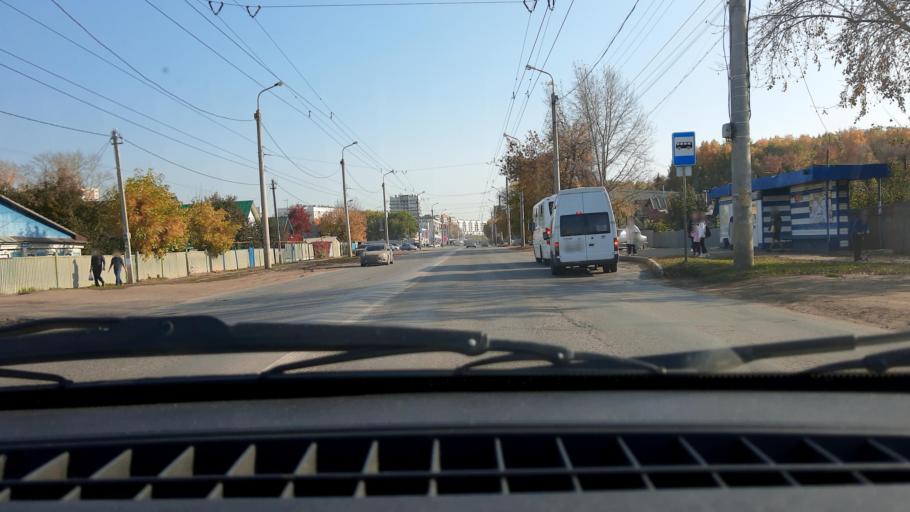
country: RU
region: Bashkortostan
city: Mikhaylovka
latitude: 54.7928
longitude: 55.8761
